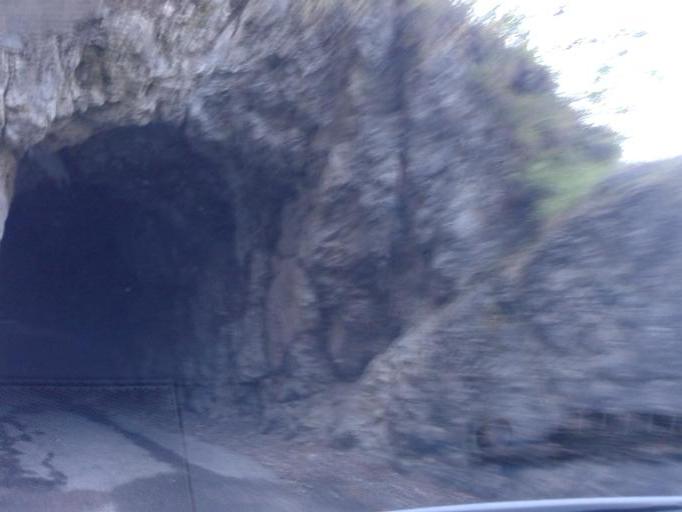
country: IT
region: Trentino-Alto Adige
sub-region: Provincia di Trento
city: Storo
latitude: 45.8528
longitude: 10.5810
